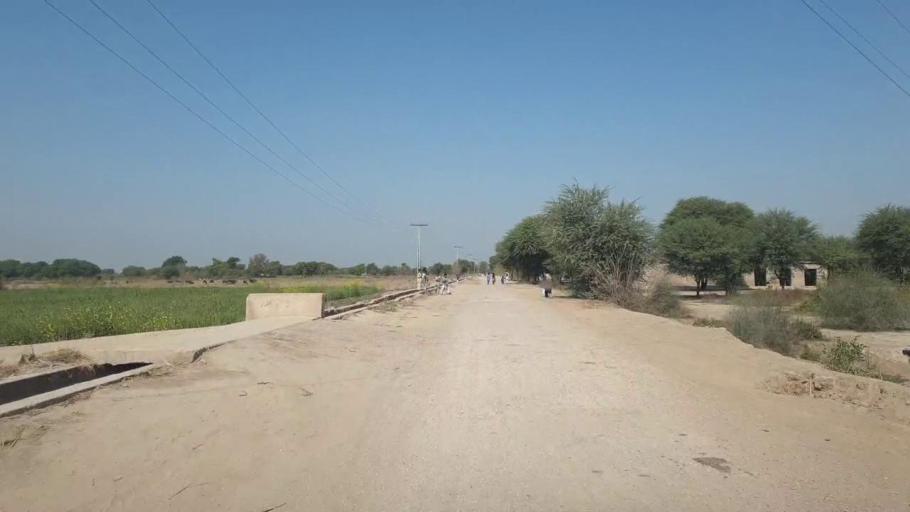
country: PK
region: Sindh
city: Chambar
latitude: 25.2927
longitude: 68.6918
